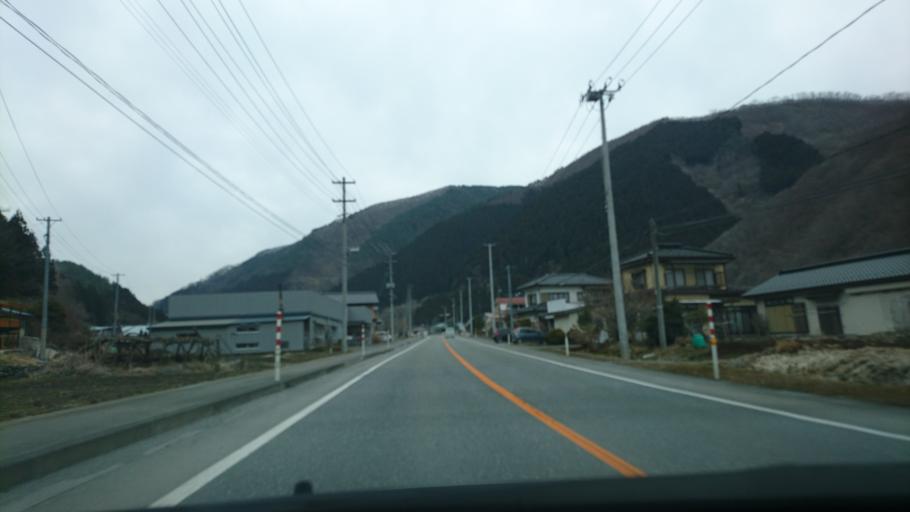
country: JP
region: Iwate
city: Tono
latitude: 39.1567
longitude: 141.5411
